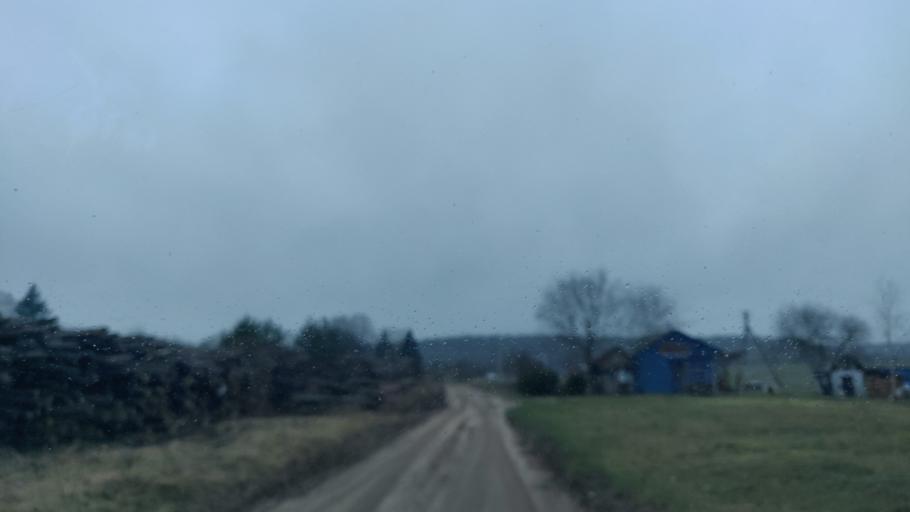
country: LT
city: Trakai
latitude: 54.5592
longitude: 24.9333
